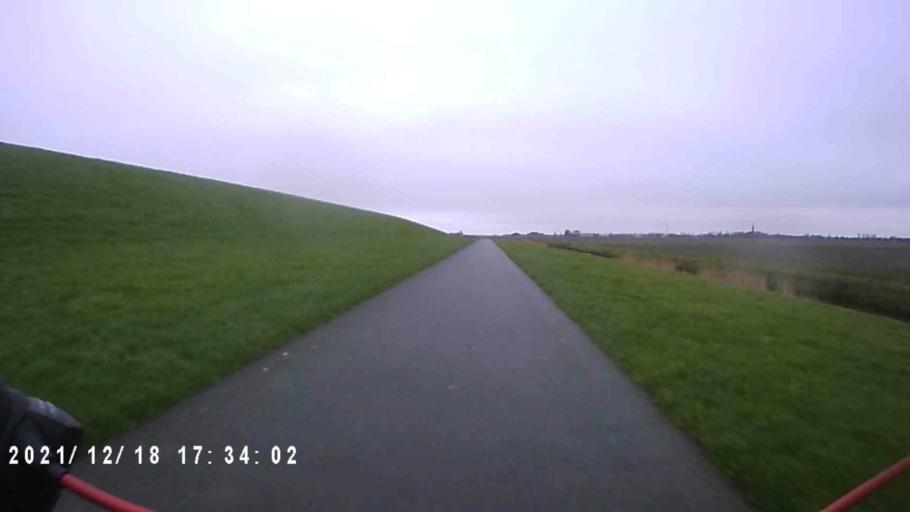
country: NL
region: Friesland
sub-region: Gemeente Dongeradeel
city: Holwerd
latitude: 53.3728
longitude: 5.8697
